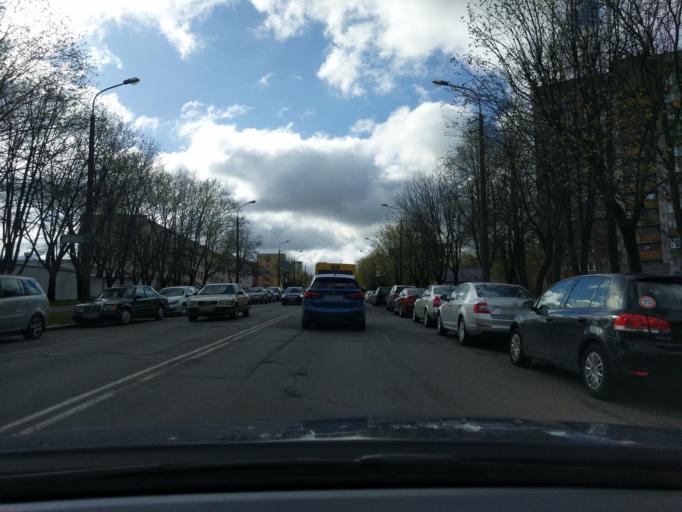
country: BY
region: Minsk
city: Novoye Medvezhino
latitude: 53.9165
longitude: 27.5029
